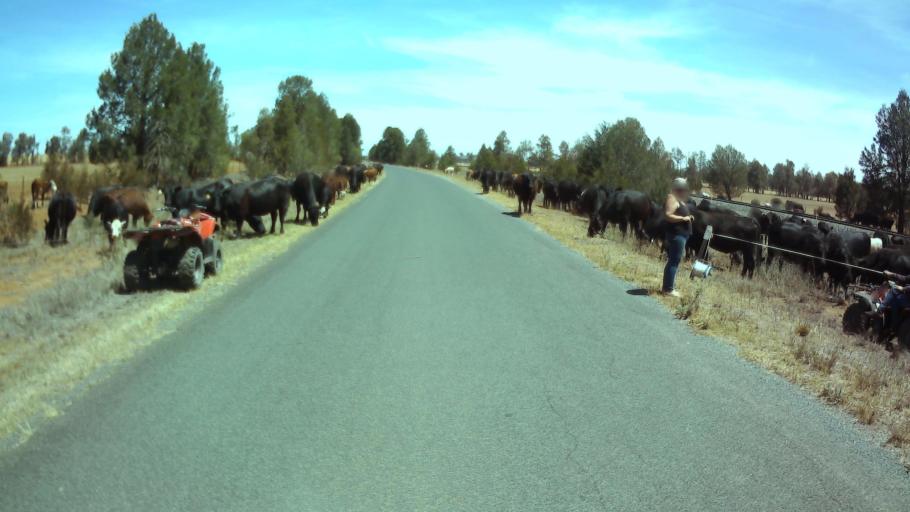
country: AU
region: New South Wales
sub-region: Weddin
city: Grenfell
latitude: -33.7785
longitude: 147.7539
